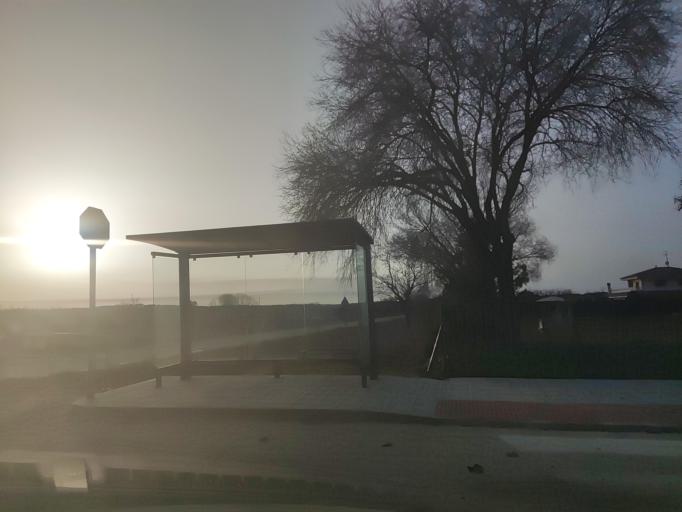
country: ES
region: Castille and Leon
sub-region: Provincia de Salamanca
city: Ciudad Rodrigo
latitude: 40.6071
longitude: -6.5610
